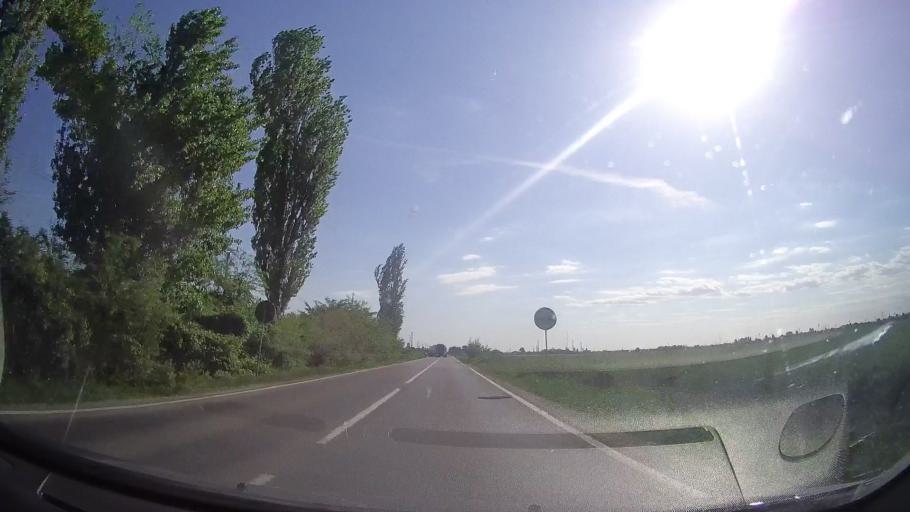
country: RO
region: Prahova
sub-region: Comuna Berceni
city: Corlatesti
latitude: 44.9083
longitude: 26.0781
